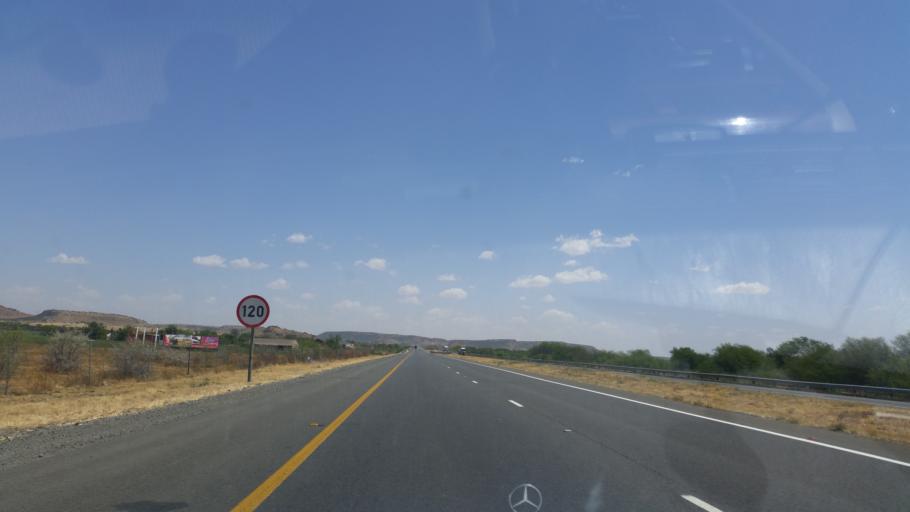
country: ZA
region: Orange Free State
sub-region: Mangaung Metropolitan Municipality
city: Bloemfontein
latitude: -28.9673
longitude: 26.3388
